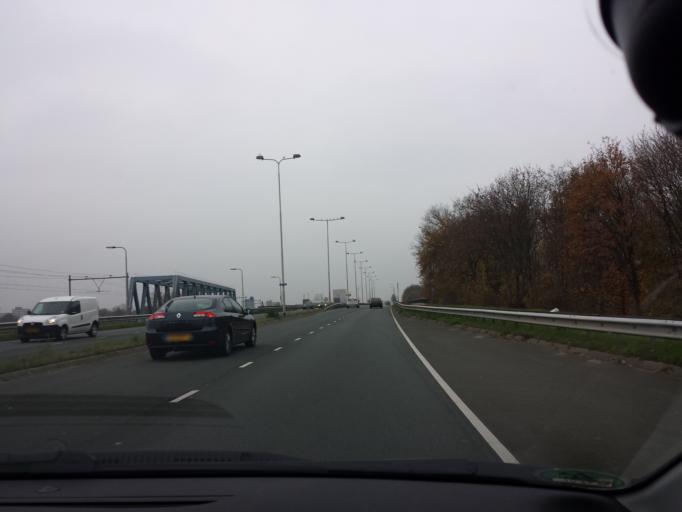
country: NL
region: Gelderland
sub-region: Gemeente Nijmegen
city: Lindenholt
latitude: 51.8263
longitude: 5.8111
